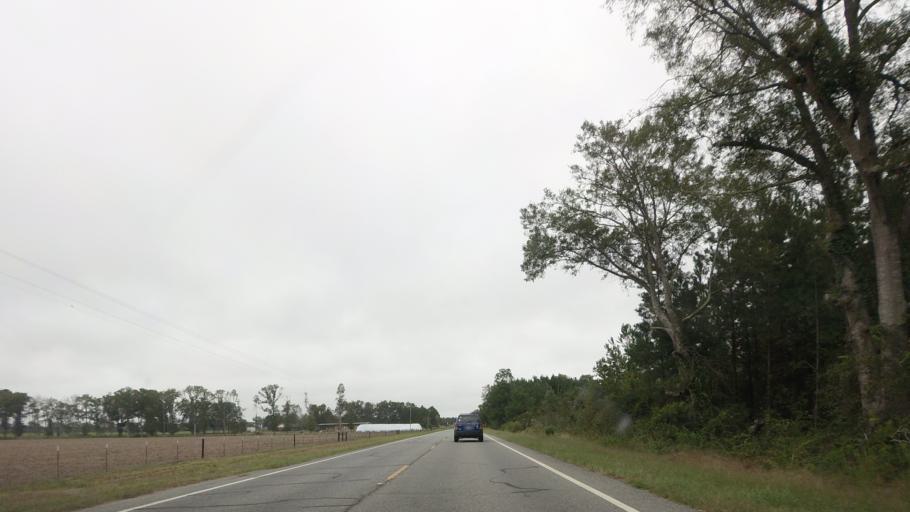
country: US
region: Georgia
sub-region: Irwin County
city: Ocilla
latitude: 31.5692
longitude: -83.2530
